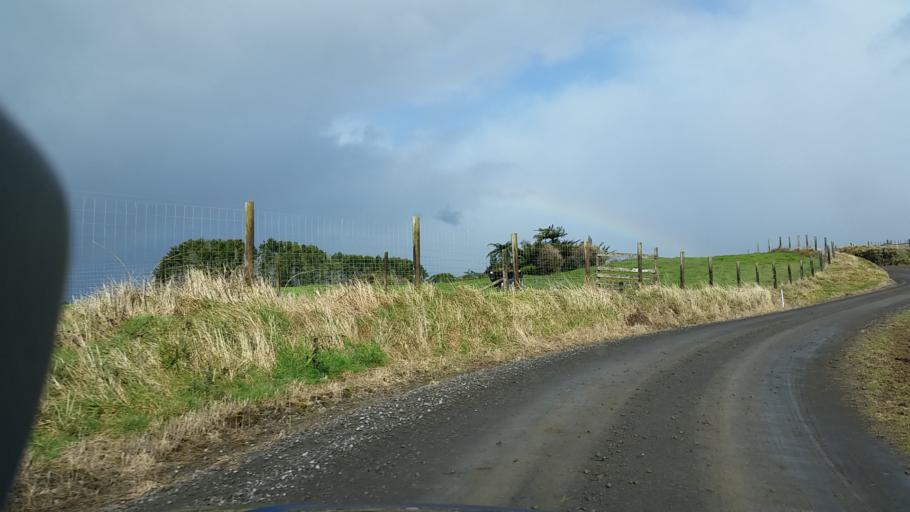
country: NZ
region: Taranaki
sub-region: South Taranaki District
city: Eltham
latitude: -39.2800
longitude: 174.3084
